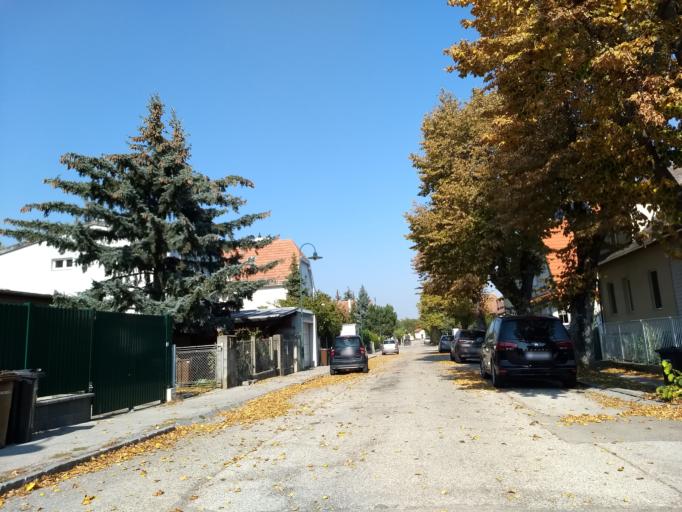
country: AT
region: Lower Austria
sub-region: Politischer Bezirk Modling
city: Brunn am Gebirge
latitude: 48.1120
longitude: 16.2807
